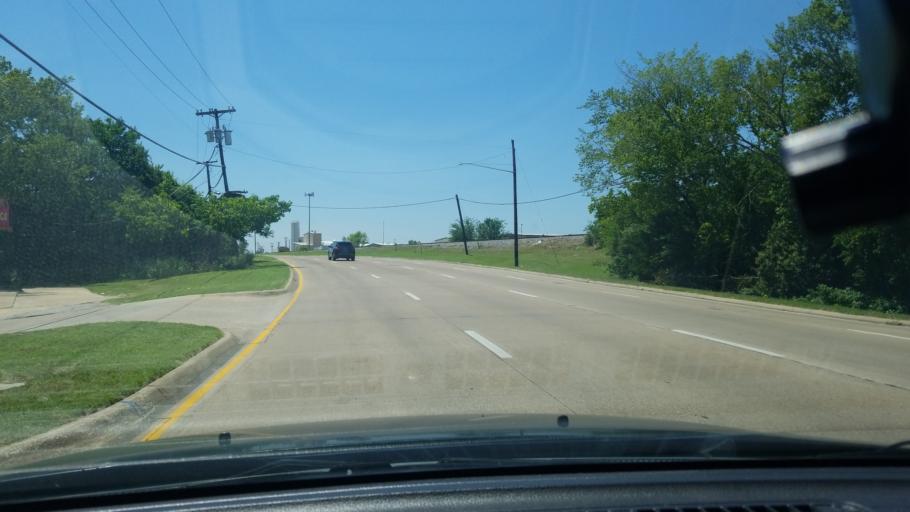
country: US
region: Texas
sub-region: Dallas County
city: Mesquite
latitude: 32.7677
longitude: -96.6065
